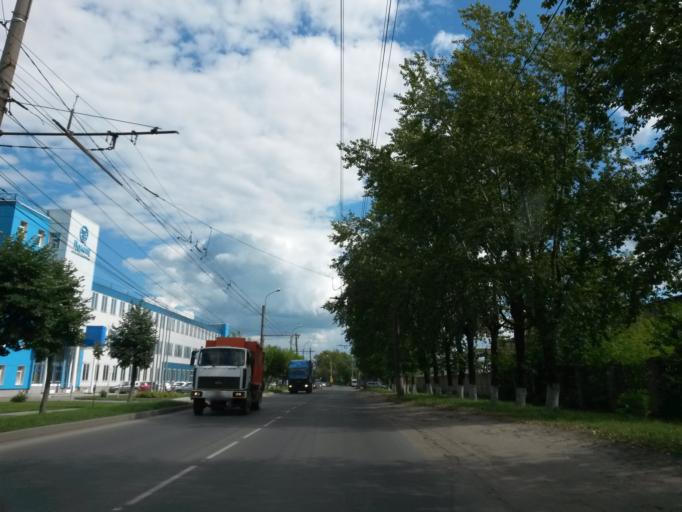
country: RU
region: Ivanovo
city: Novo-Talitsy
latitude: 56.9989
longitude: 40.9103
